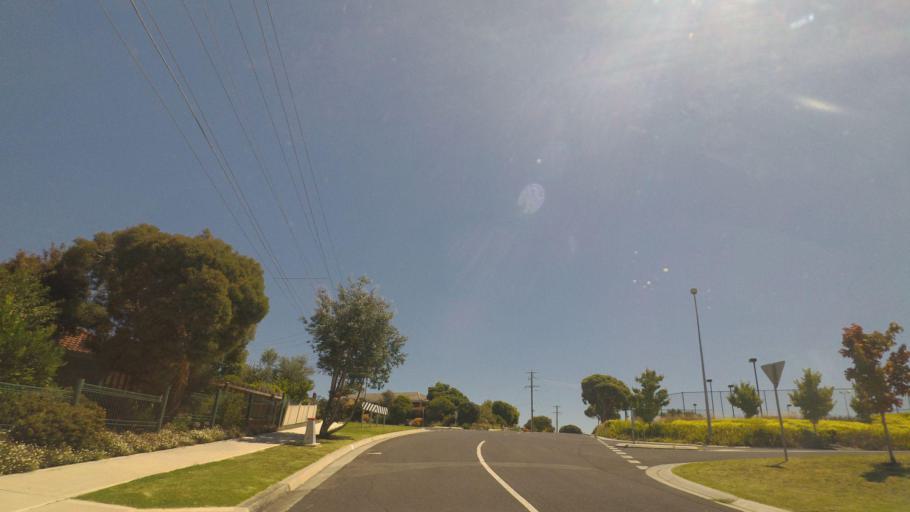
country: AU
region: Victoria
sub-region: Yarra Ranges
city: Chirnside Park
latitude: -37.7510
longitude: 145.3268
